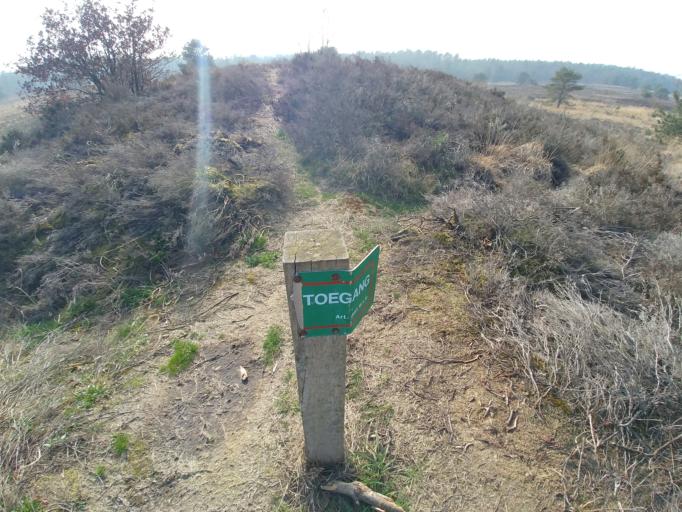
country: NL
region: Gelderland
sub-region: Gemeente Epe
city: Emst
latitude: 52.3195
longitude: 5.8915
